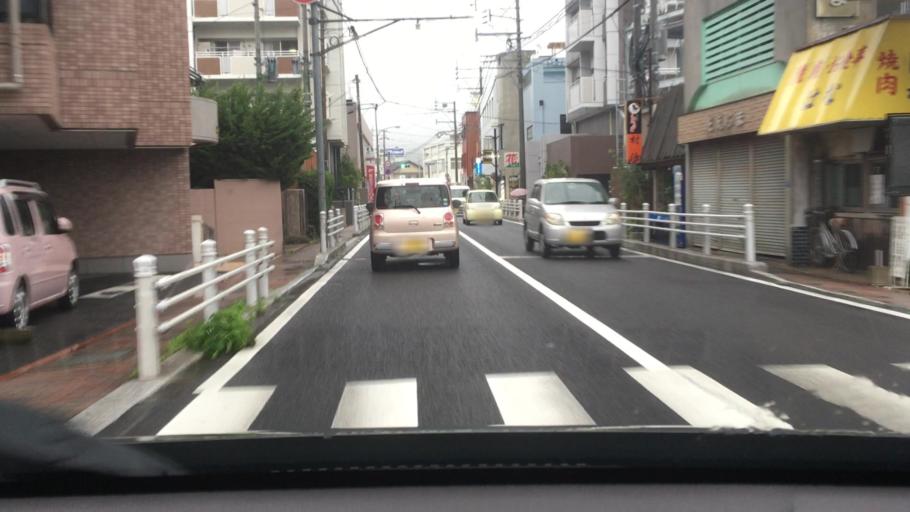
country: JP
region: Nagasaki
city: Sasebo
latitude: 33.1347
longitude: 129.7984
